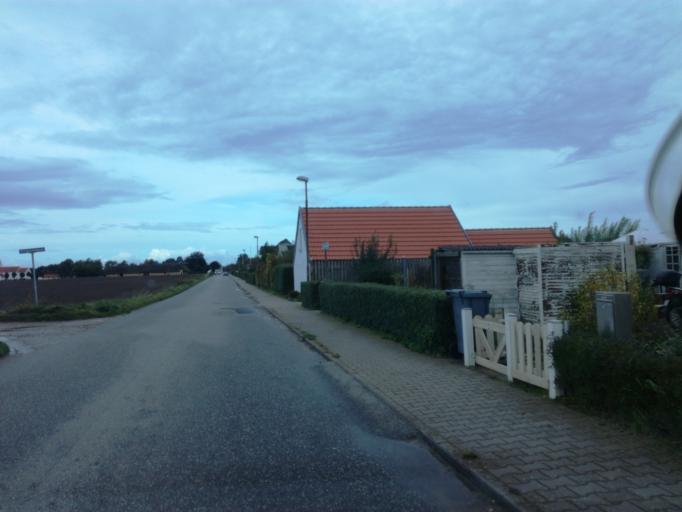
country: DK
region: South Denmark
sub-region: Fredericia Kommune
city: Fredericia
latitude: 55.6098
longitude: 9.7457
